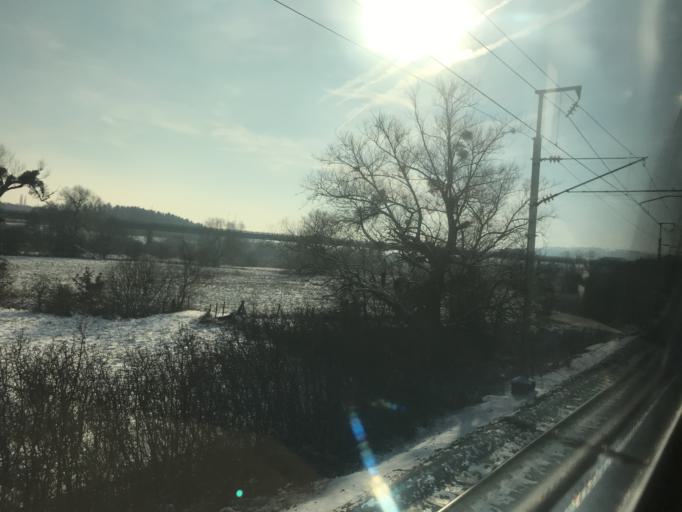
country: LU
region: Luxembourg
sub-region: Canton de Luxembourg
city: Niederanven
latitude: 49.6453
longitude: 6.2806
